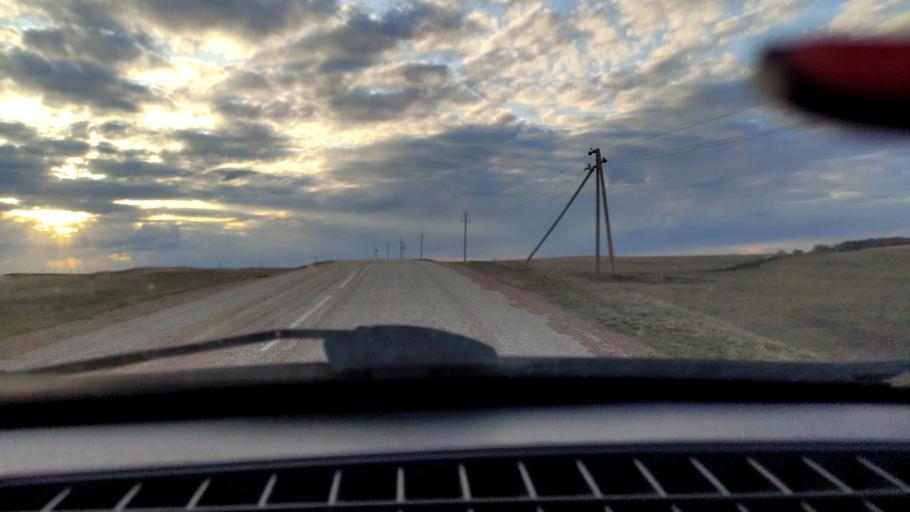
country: RU
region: Bashkortostan
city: Tolbazy
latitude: 54.0030
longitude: 55.6519
